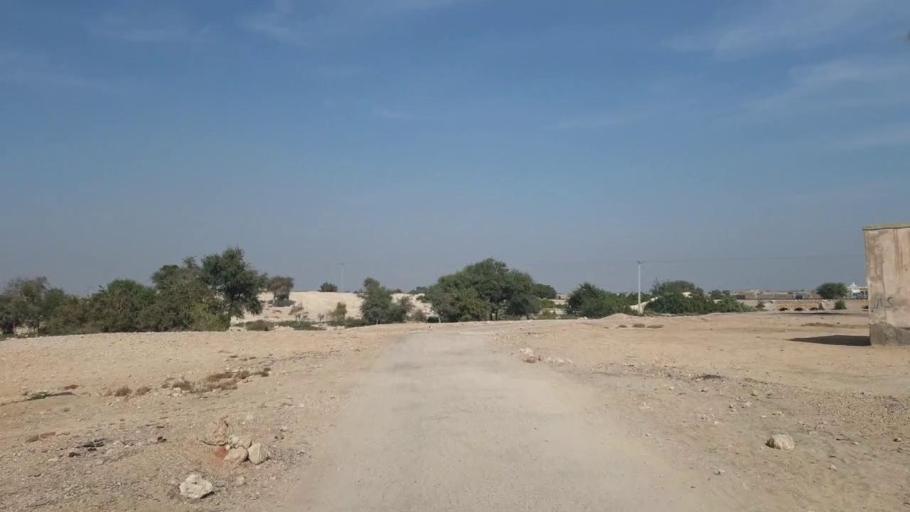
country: PK
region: Sindh
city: Hala
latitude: 25.7659
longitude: 68.2903
